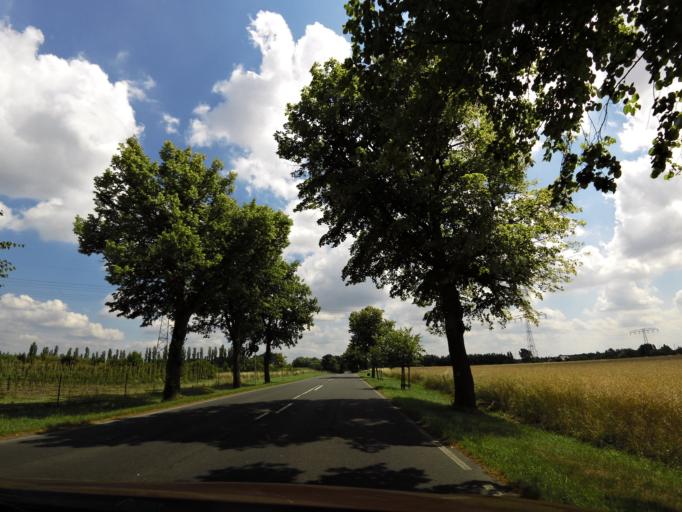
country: DE
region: Brandenburg
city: Nauen
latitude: 52.6115
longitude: 12.8484
